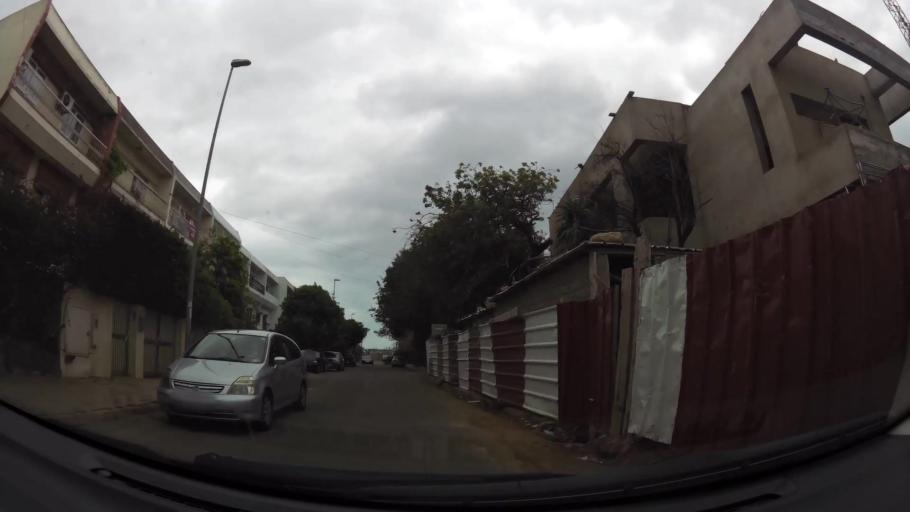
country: MA
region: Grand Casablanca
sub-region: Casablanca
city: Casablanca
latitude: 33.5700
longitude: -7.6559
